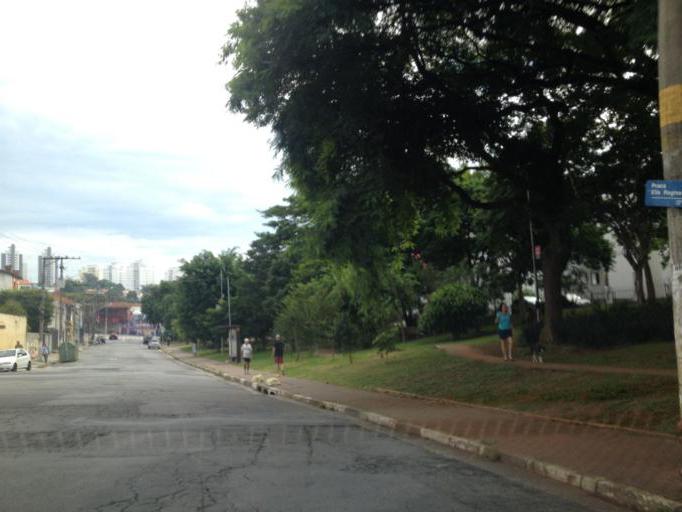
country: BR
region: Sao Paulo
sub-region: Osasco
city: Osasco
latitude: -23.5765
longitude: -46.7304
